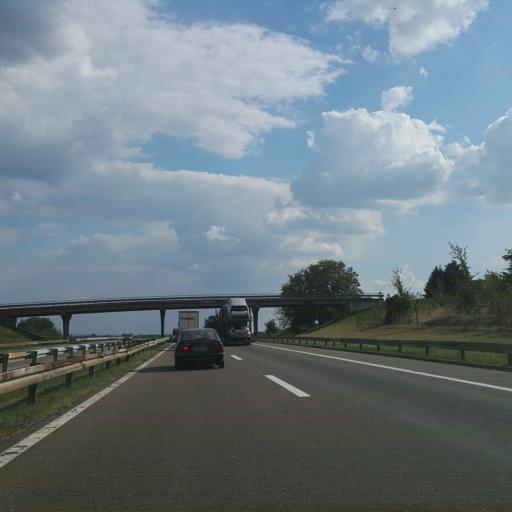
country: RS
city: Lugavcina
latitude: 44.4451
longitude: 21.0472
